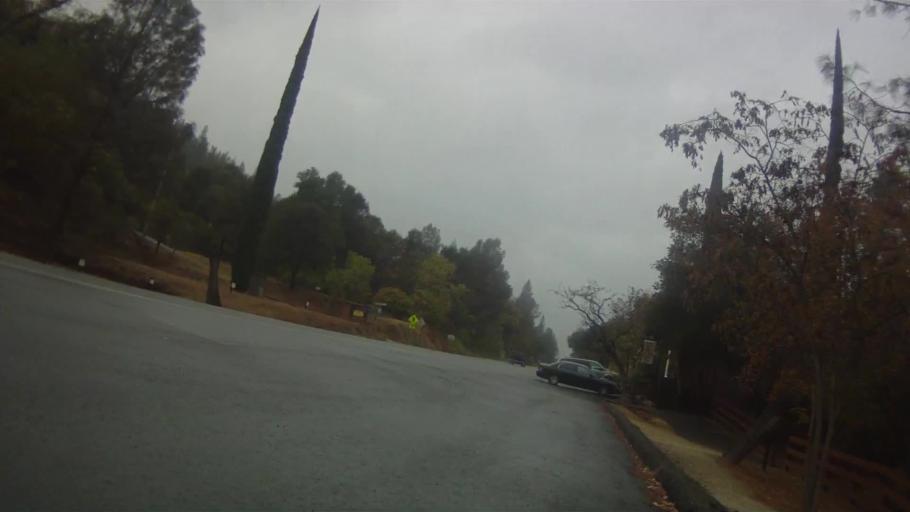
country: US
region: California
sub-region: Shasta County
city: Shasta
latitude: 40.5988
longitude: -122.4916
